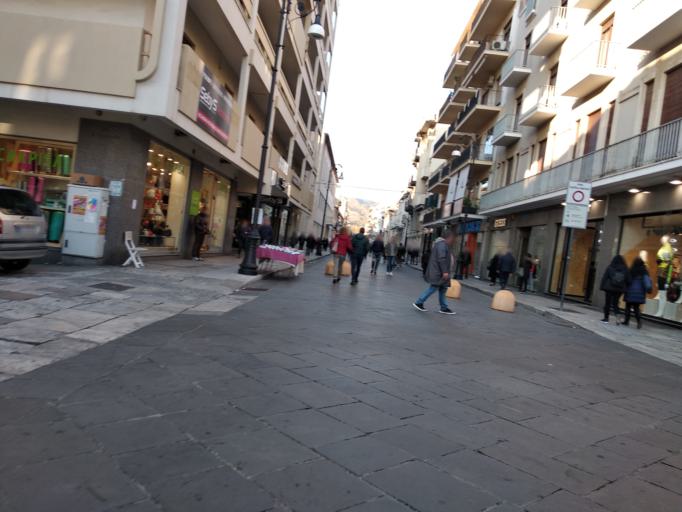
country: IT
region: Calabria
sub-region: Provincia di Reggio Calabria
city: Reggio Calabria
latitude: 38.1113
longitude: 15.6474
